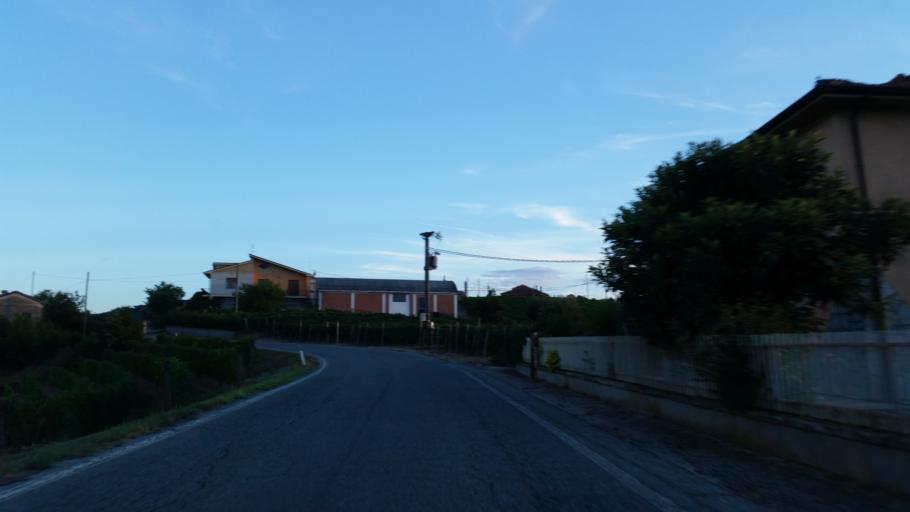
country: IT
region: Piedmont
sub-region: Provincia di Cuneo
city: Castiglione Tinella
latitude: 44.7380
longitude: 8.1962
